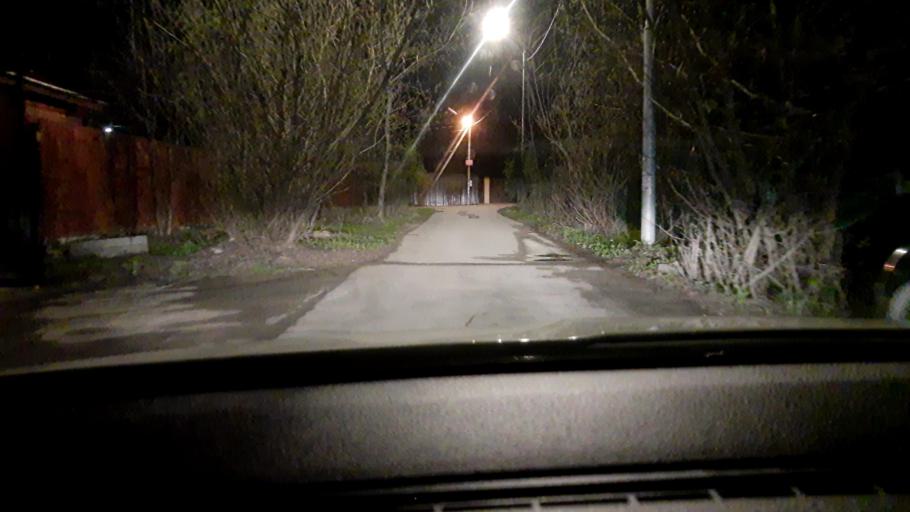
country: RU
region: Moskovskaya
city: Annino
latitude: 55.6190
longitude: 37.2567
